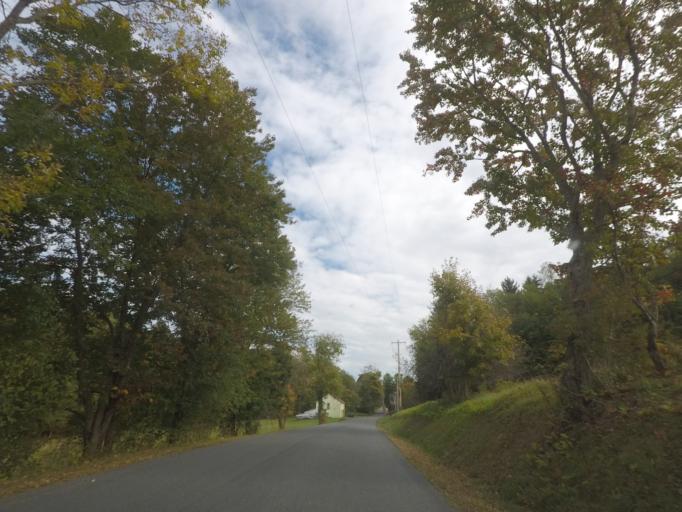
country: US
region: New York
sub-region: Rensselaer County
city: Nassau
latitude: 42.5462
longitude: -73.6309
